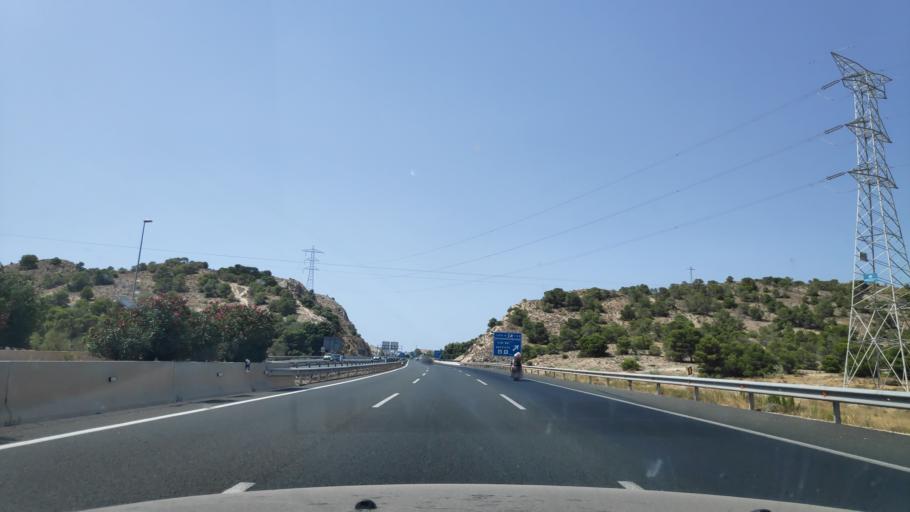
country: ES
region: Murcia
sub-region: Murcia
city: Murcia
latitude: 37.8709
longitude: -1.1249
